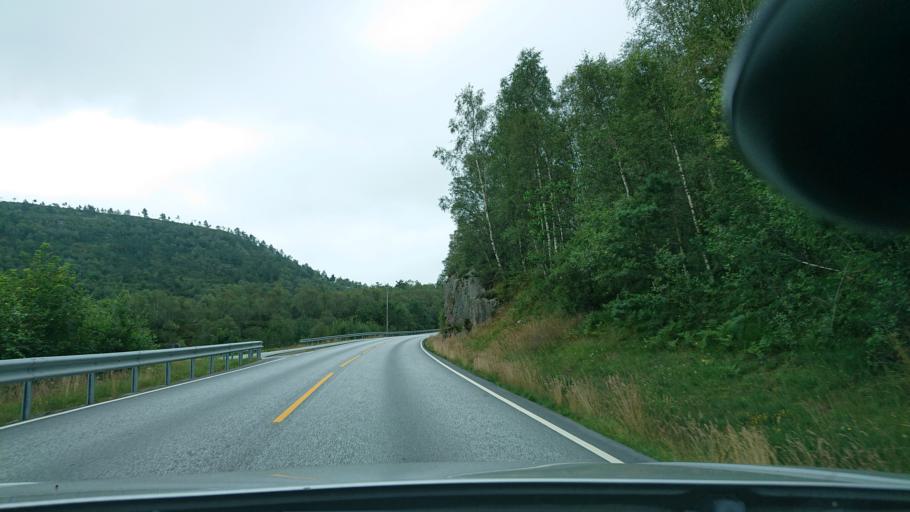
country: NO
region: Rogaland
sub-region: Hjelmeland
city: Hjelmelandsvagen
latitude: 59.1684
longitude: 6.1577
